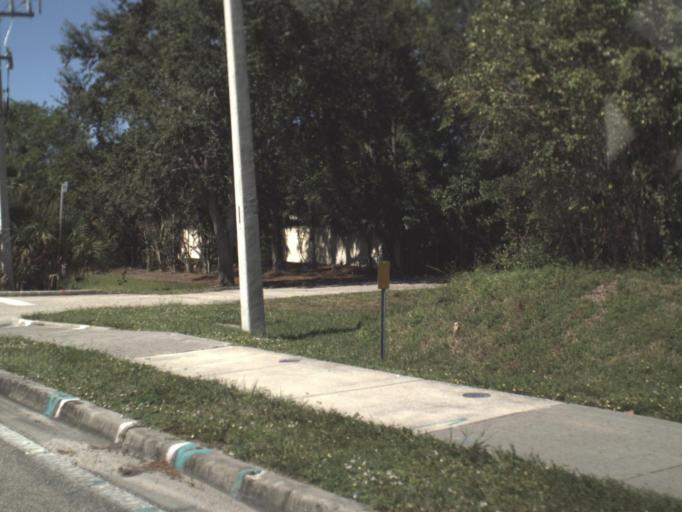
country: US
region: Florida
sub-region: Collier County
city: Lely
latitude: 26.1389
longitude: -81.7424
